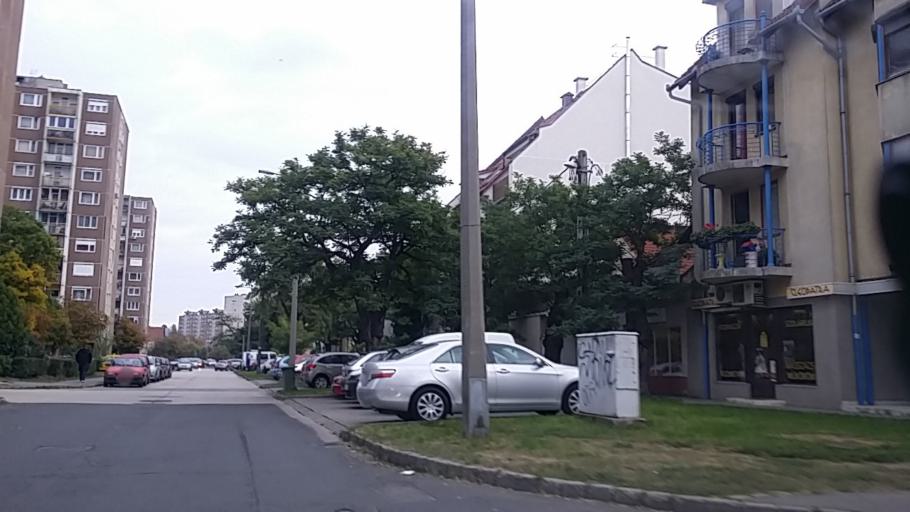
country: HU
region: Budapest
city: Budapest IV. keruelet
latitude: 47.5610
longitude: 19.0929
